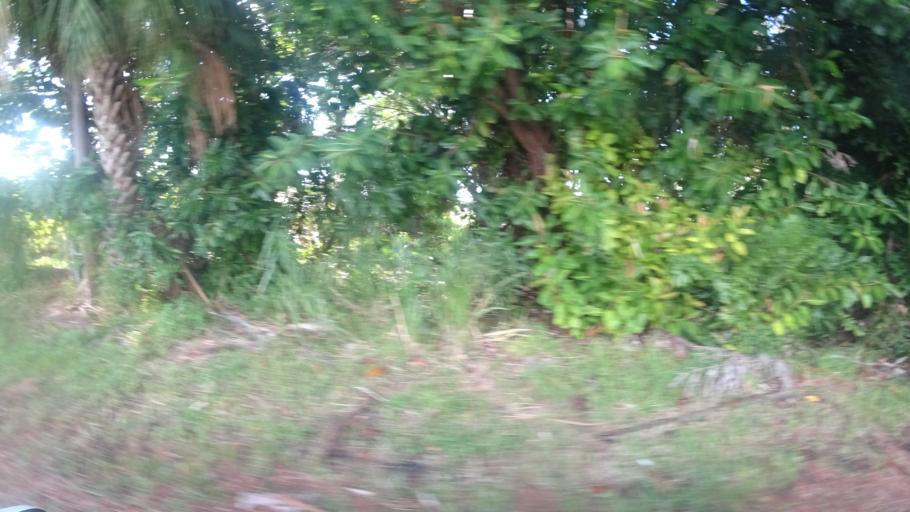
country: US
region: Florida
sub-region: Manatee County
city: West Bradenton
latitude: 27.5282
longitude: -82.6159
